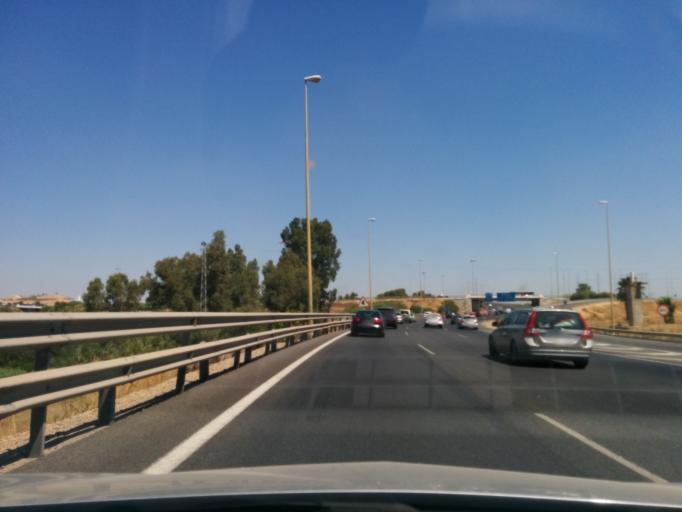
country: ES
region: Andalusia
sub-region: Provincia de Sevilla
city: Camas
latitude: 37.3852
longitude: -6.0256
